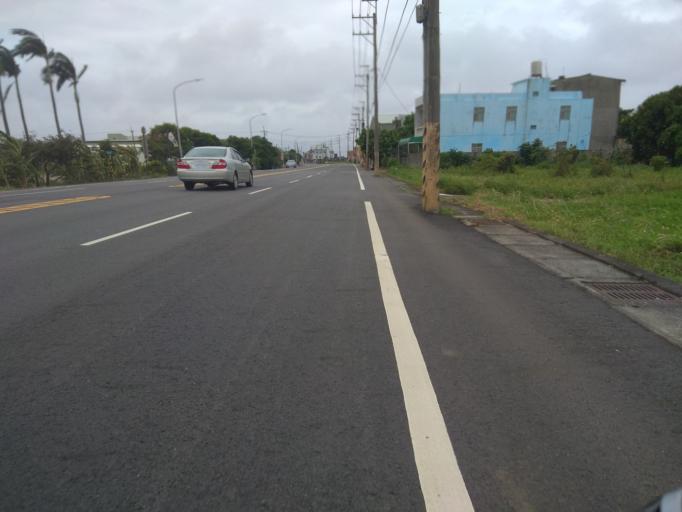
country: TW
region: Taiwan
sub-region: Hsinchu
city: Zhubei
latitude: 24.9804
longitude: 121.0694
